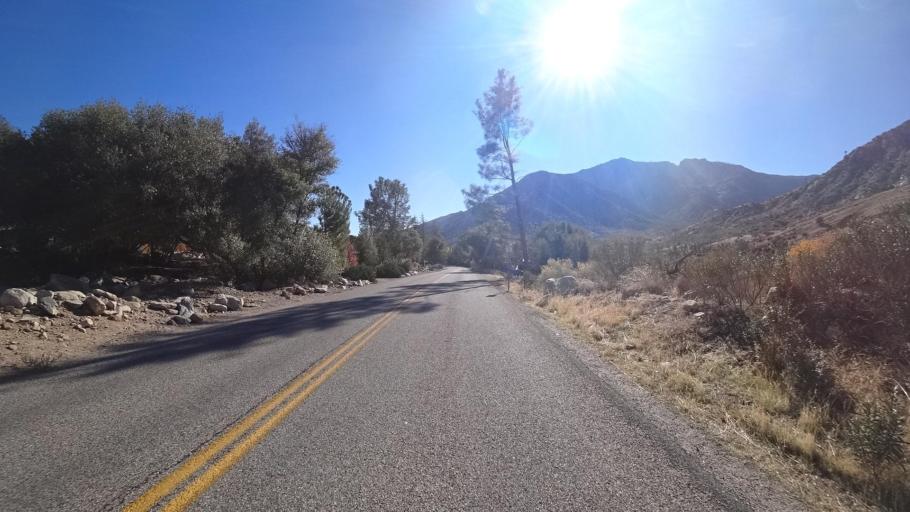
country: US
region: California
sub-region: Kern County
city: Kernville
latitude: 35.7909
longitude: -118.4478
